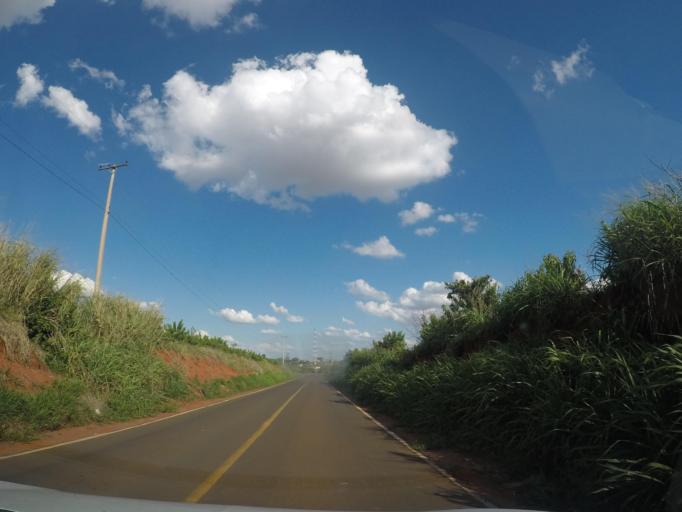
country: BR
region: Sao Paulo
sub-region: Sumare
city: Sumare
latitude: -22.8620
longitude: -47.2954
